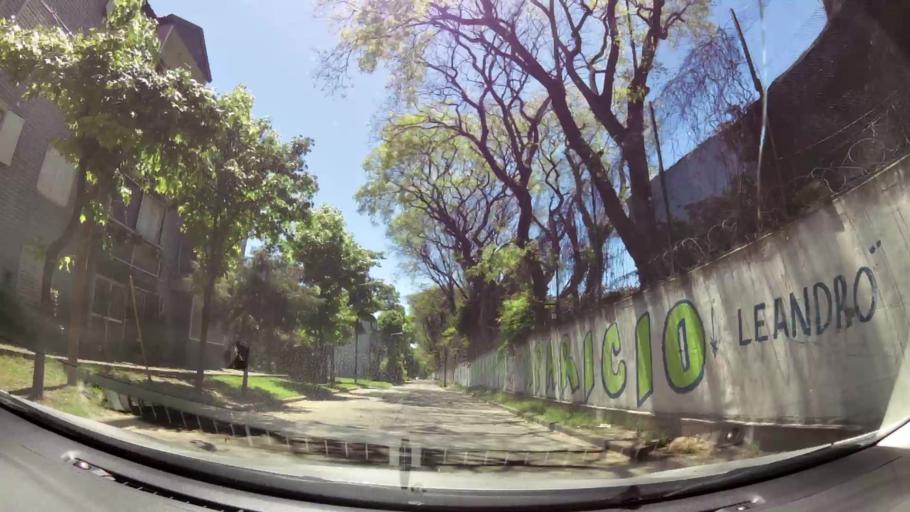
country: AR
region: Buenos Aires
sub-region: Partido de Tigre
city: Tigre
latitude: -34.4622
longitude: -58.5610
